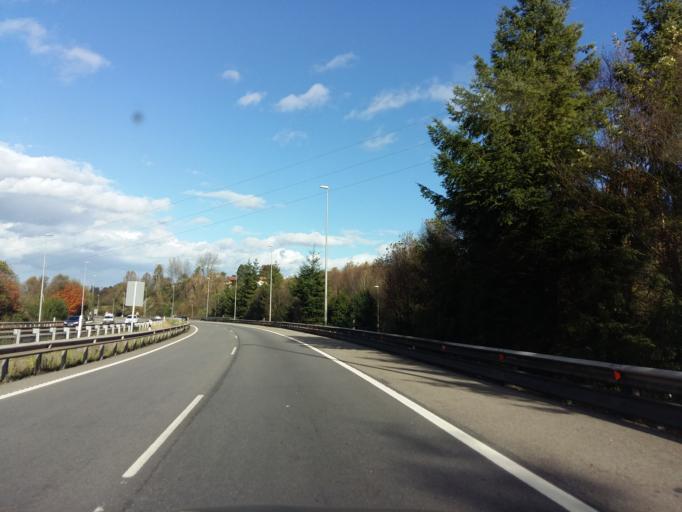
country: ES
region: Asturias
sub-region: Province of Asturias
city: Oviedo
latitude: 43.3532
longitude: -5.8296
